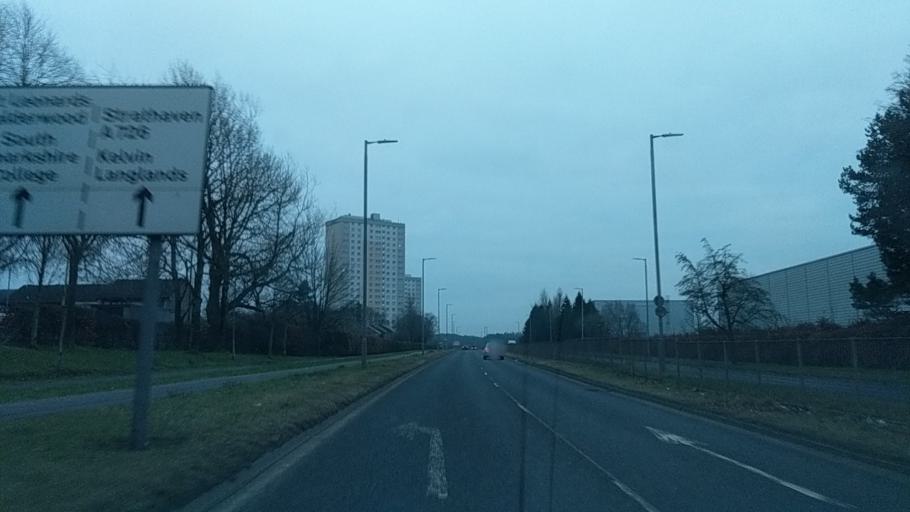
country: GB
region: Scotland
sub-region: South Lanarkshire
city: East Kilbride
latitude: 55.7568
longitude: -4.1627
